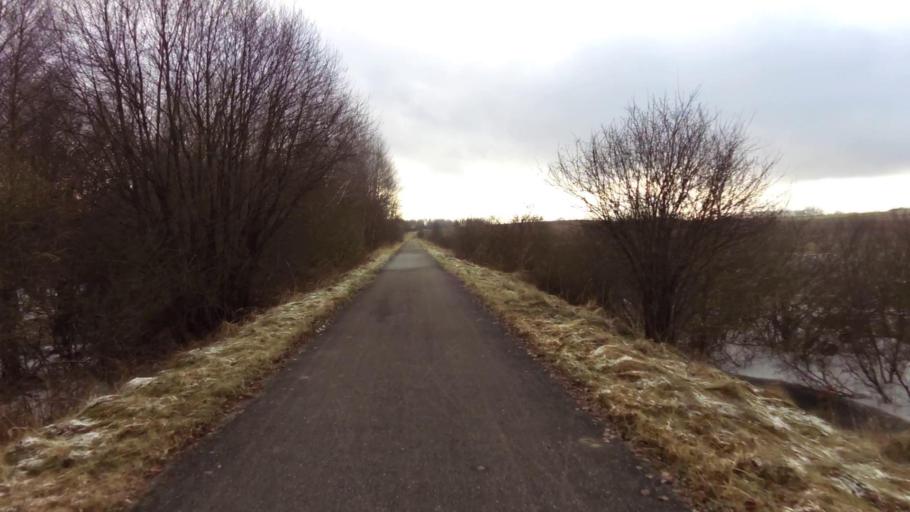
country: PL
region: West Pomeranian Voivodeship
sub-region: Powiat drawski
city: Zlocieniec
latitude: 53.6053
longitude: 16.0471
